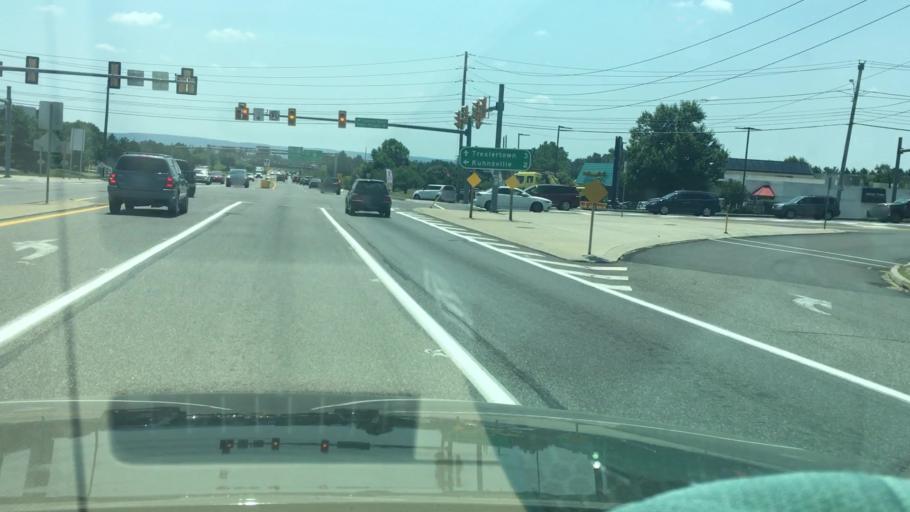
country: US
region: Pennsylvania
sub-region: Lehigh County
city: Trexlertown
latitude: 40.5850
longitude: -75.6267
